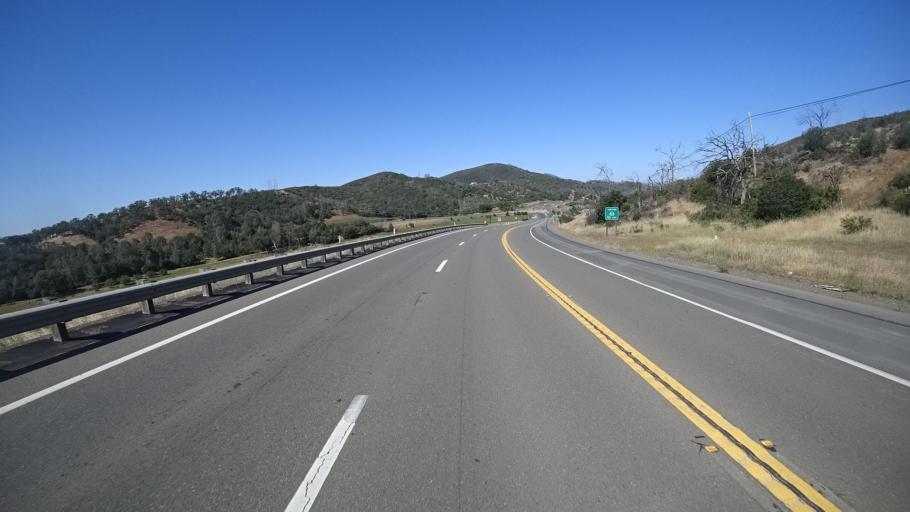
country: US
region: California
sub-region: Lake County
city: Clearlake
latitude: 39.0095
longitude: -122.6073
